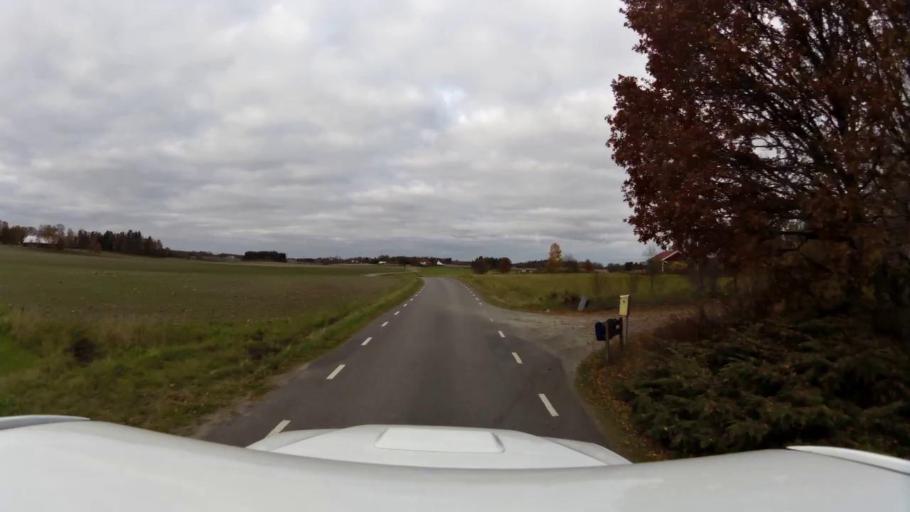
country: SE
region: OEstergoetland
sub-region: Linkopings Kommun
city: Linghem
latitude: 58.3939
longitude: 15.7987
